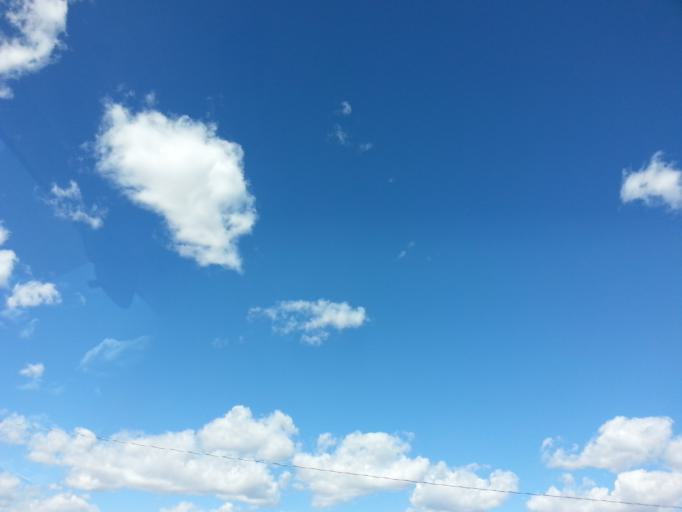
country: US
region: Minnesota
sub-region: Dakota County
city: Rosemount
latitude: 44.7103
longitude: -93.0370
